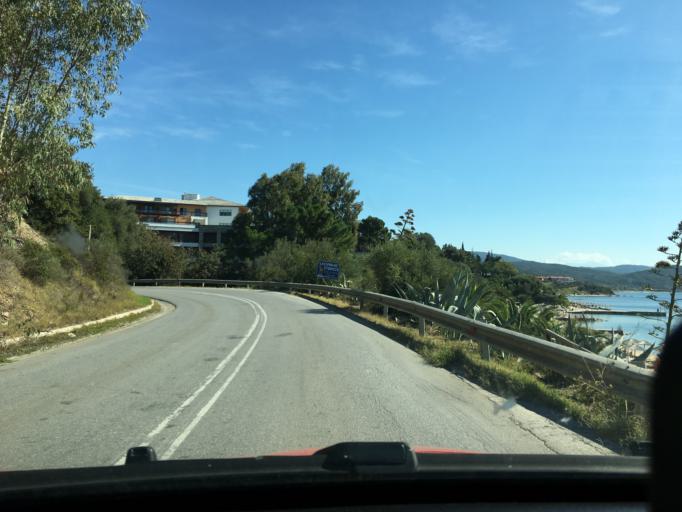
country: GR
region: Central Macedonia
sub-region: Nomos Chalkidikis
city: Nea Roda
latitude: 40.3541
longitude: 23.9490
